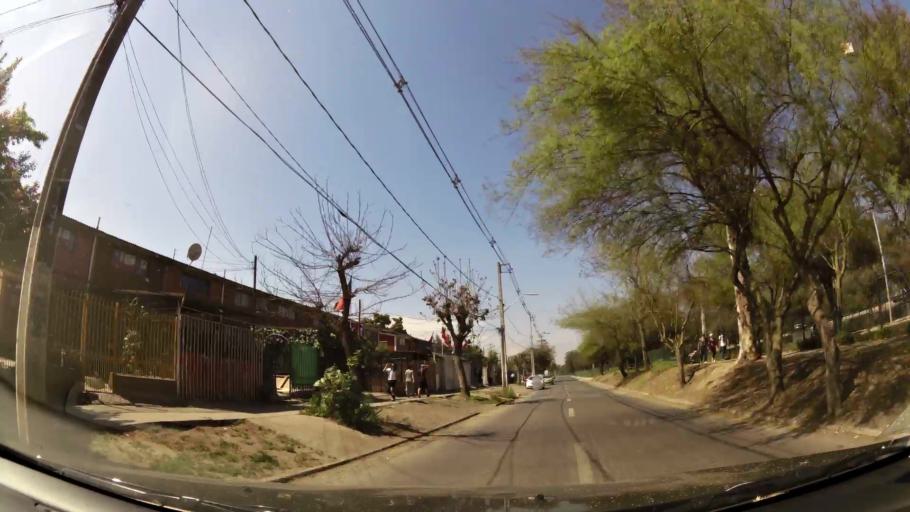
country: CL
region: Santiago Metropolitan
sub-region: Provincia de Santiago
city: Lo Prado
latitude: -33.4113
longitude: -70.7437
